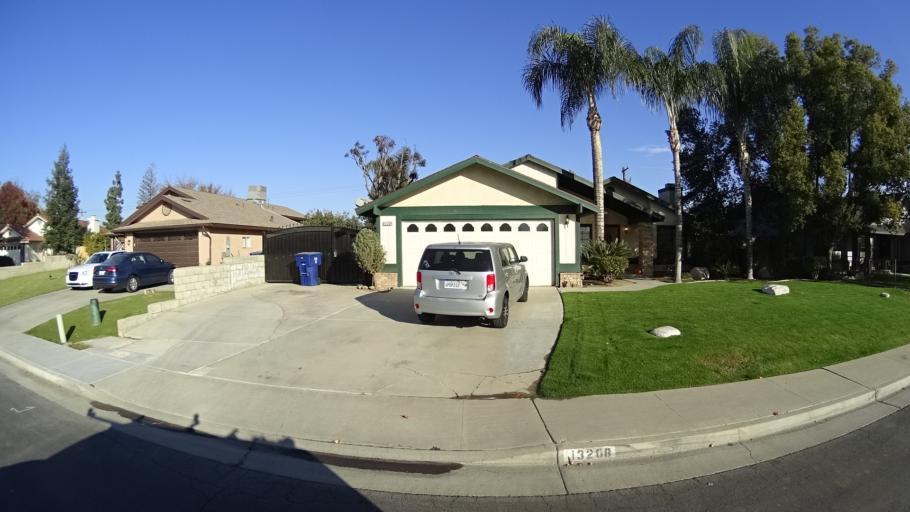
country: US
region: California
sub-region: Kern County
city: Rosedale
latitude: 35.3536
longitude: -119.1490
